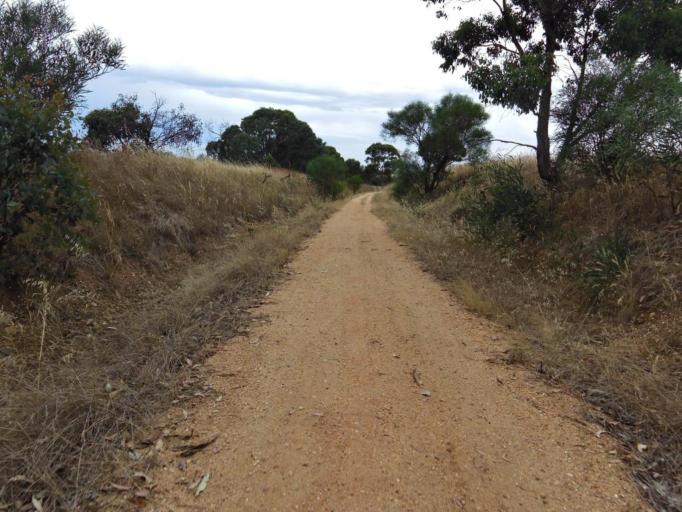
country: AU
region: Victoria
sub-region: Greater Bendigo
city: Kennington
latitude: -36.8571
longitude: 144.6205
